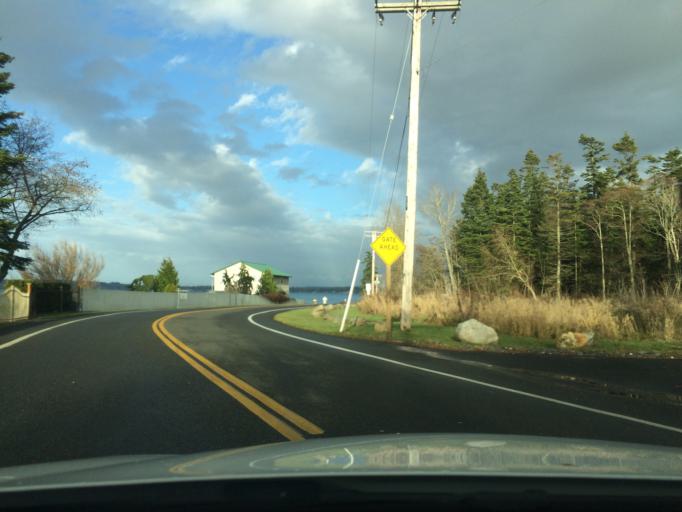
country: US
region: Washington
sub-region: Whatcom County
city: Birch Bay
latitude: 48.8998
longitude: -122.7744
